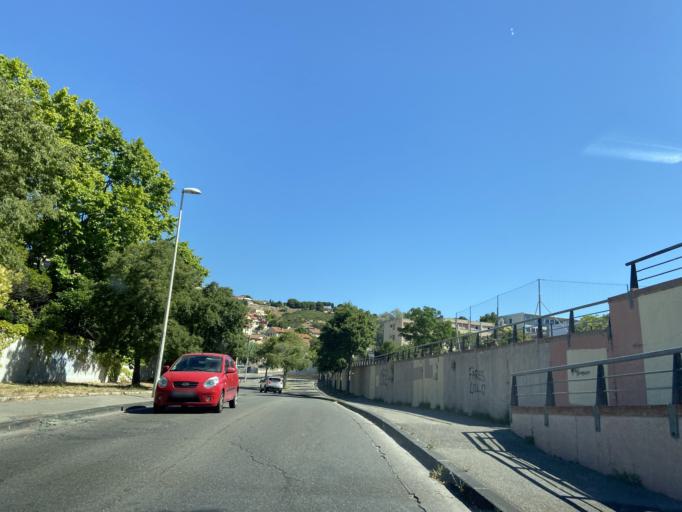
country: FR
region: Provence-Alpes-Cote d'Azur
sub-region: Departement des Bouches-du-Rhone
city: Marseille 15
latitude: 43.3691
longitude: 5.3463
